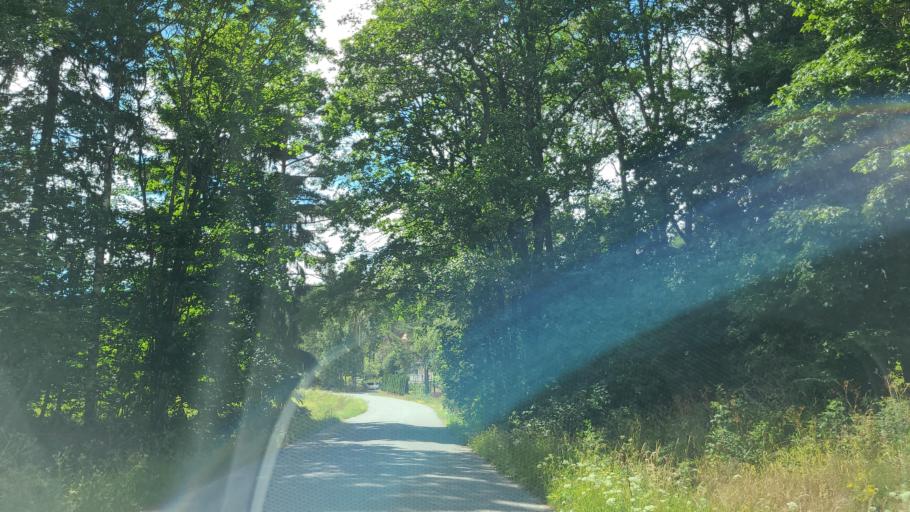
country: FI
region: Varsinais-Suomi
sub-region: Aboland-Turunmaa
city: Nagu
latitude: 60.1684
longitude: 22.0436
